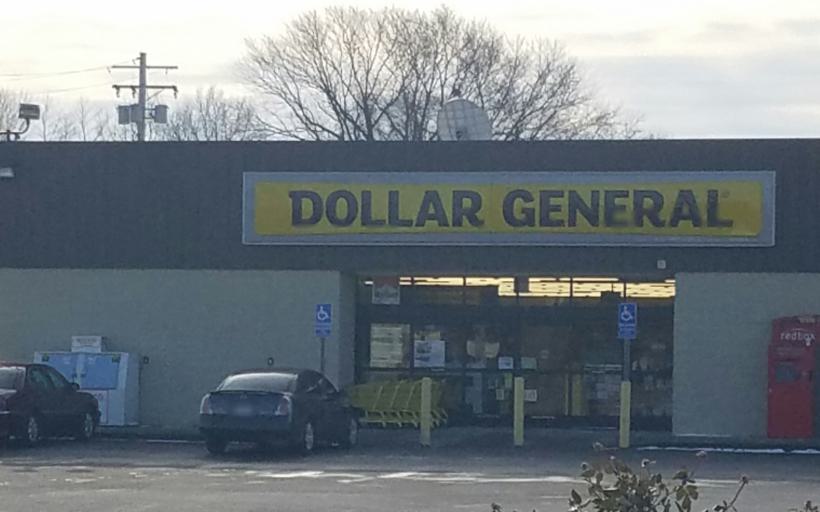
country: US
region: Missouri
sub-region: Moniteau County
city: Tipton
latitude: 38.6540
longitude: -92.7928
